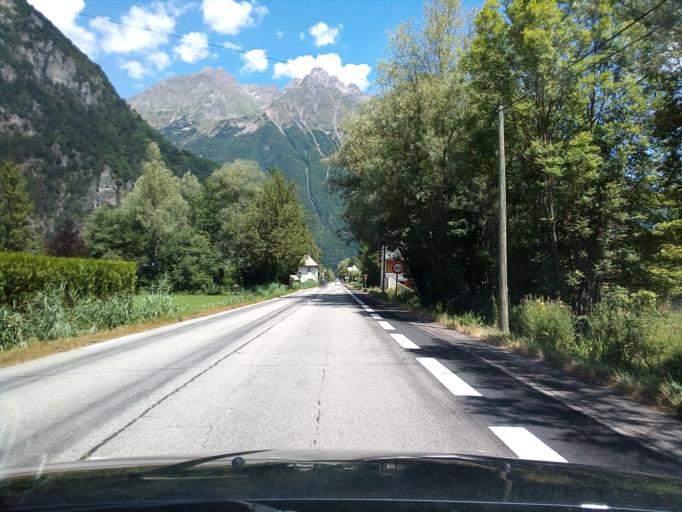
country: FR
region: Rhone-Alpes
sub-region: Departement de l'Isere
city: Huez
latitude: 45.1022
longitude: 6.0087
